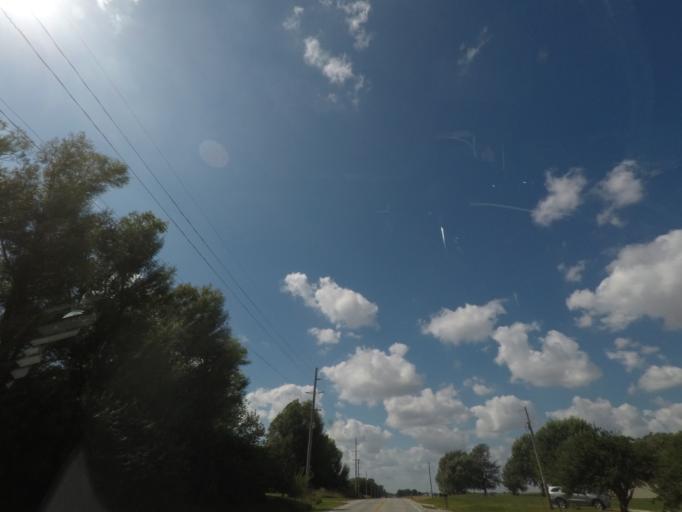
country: US
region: Iowa
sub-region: Story County
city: Nevada
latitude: 42.0227
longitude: -93.4175
